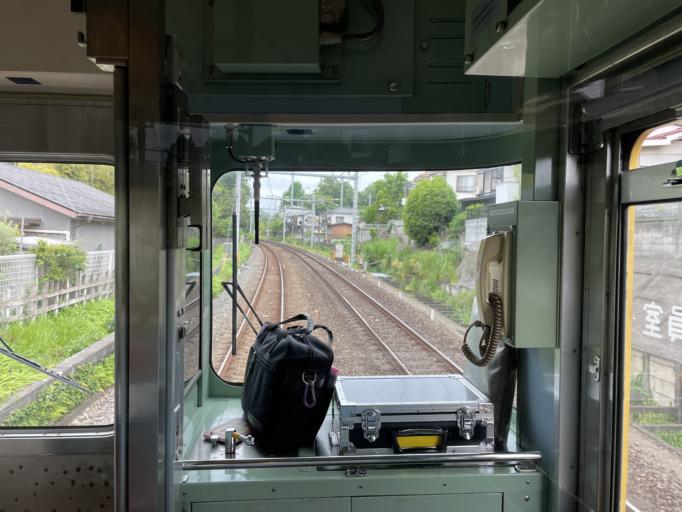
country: JP
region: Saitama
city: Hanno
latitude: 35.8419
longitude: 139.3415
